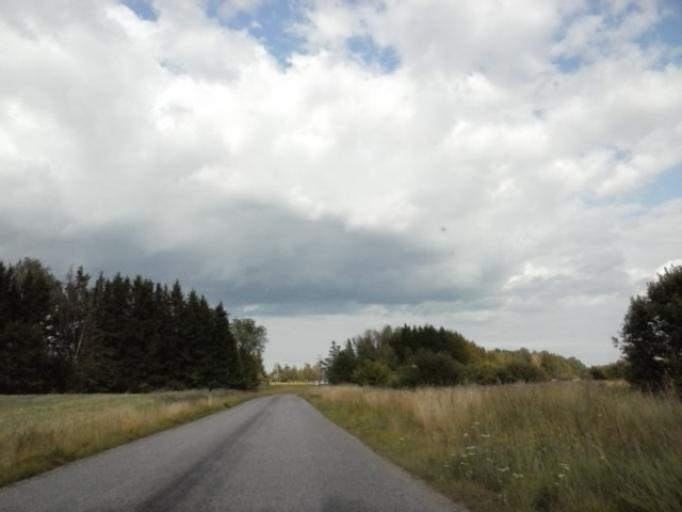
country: EE
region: Vorumaa
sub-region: Voru linn
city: Voru
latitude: 57.8391
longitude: 27.1561
